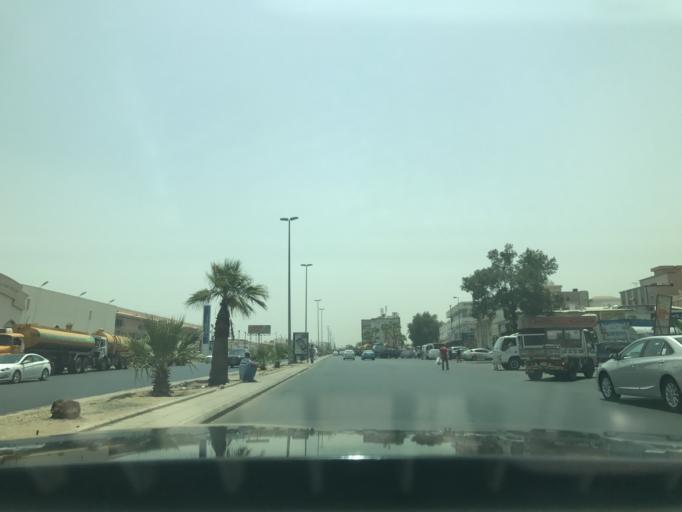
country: SA
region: Makkah
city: Jeddah
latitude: 21.5685
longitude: 39.1847
